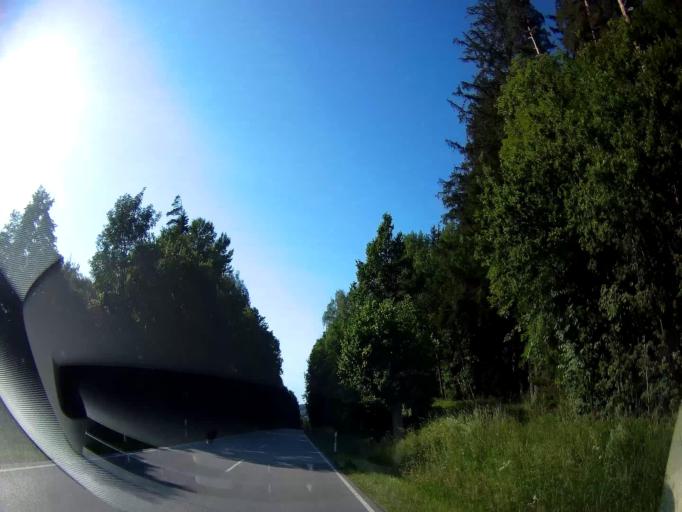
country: DE
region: Bavaria
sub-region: Lower Bavaria
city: Eggenfelden
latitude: 48.3823
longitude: 12.7761
